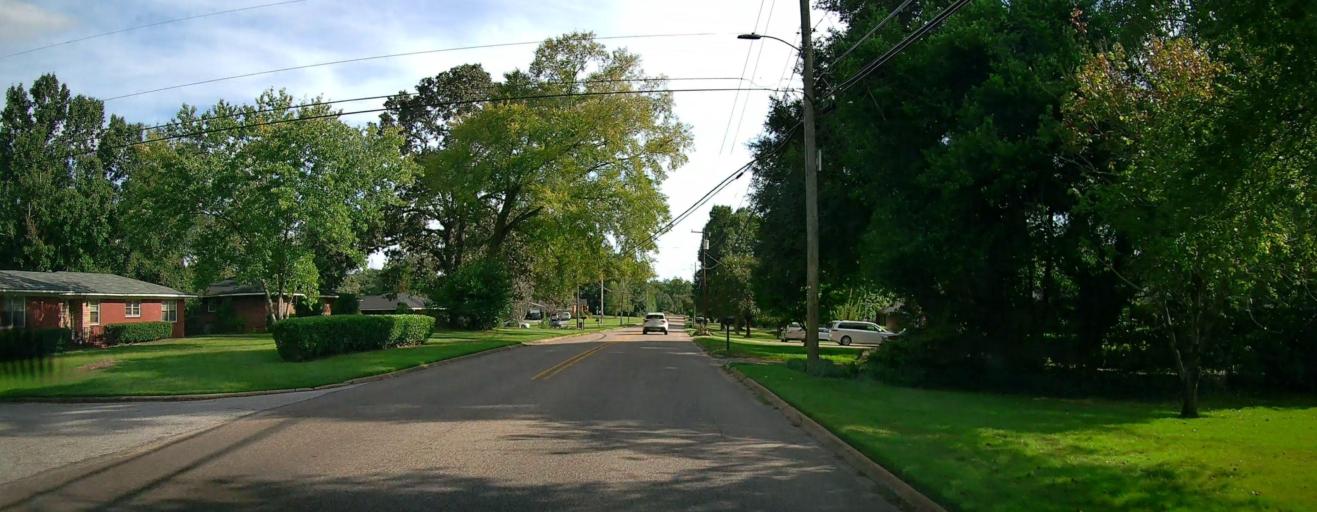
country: US
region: Alabama
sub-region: Russell County
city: Phenix City
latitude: 32.5082
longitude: -85.0196
